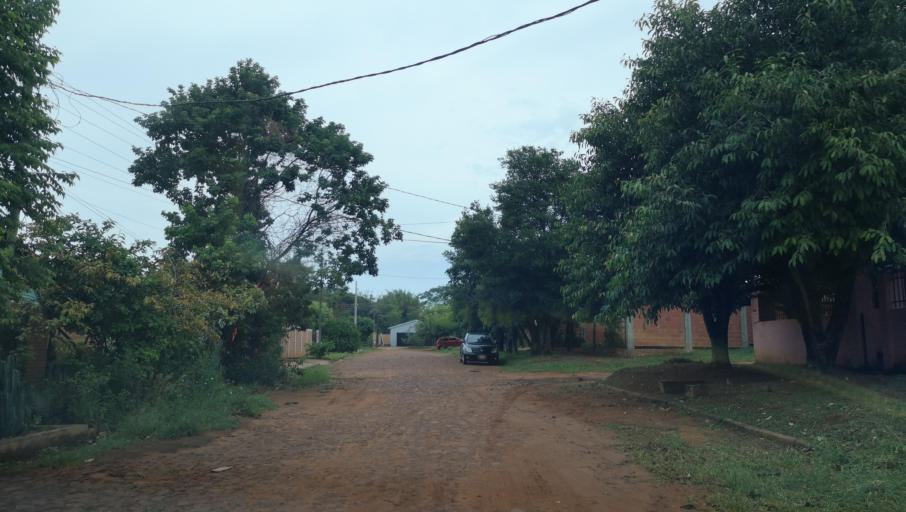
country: PY
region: Misiones
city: Santa Maria
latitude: -26.8819
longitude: -57.0338
